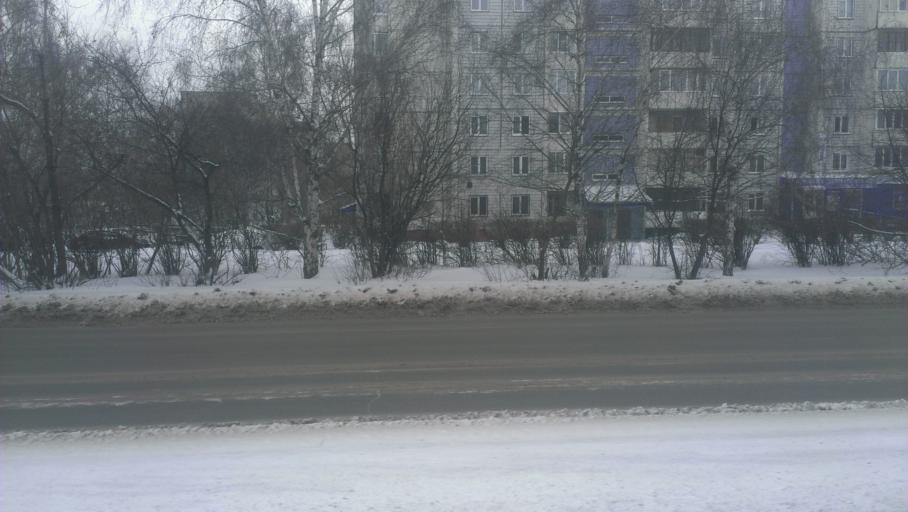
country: RU
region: Altai Krai
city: Novosilikatnyy
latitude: 53.3607
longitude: 83.6745
